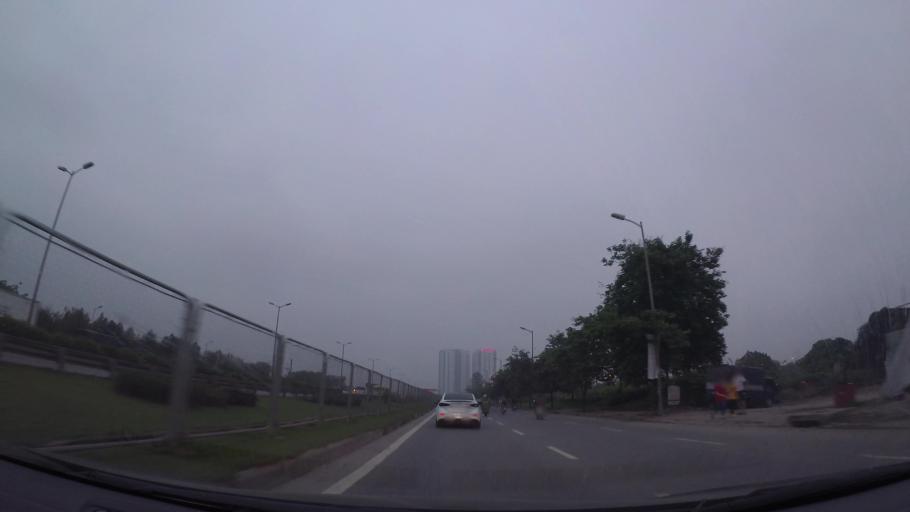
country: VN
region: Ha Noi
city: Van Dien
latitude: 20.9645
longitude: 105.8573
